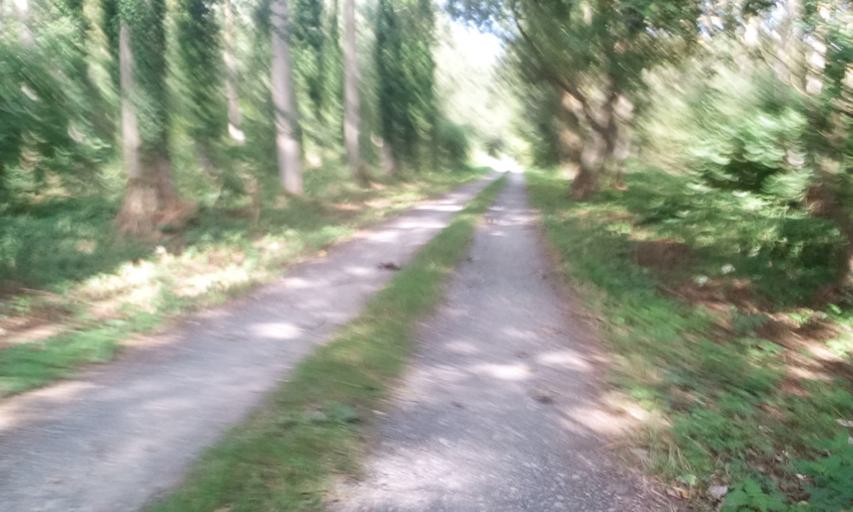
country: FR
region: Lower Normandy
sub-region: Departement du Calvados
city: Argences
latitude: 49.1384
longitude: -0.1712
